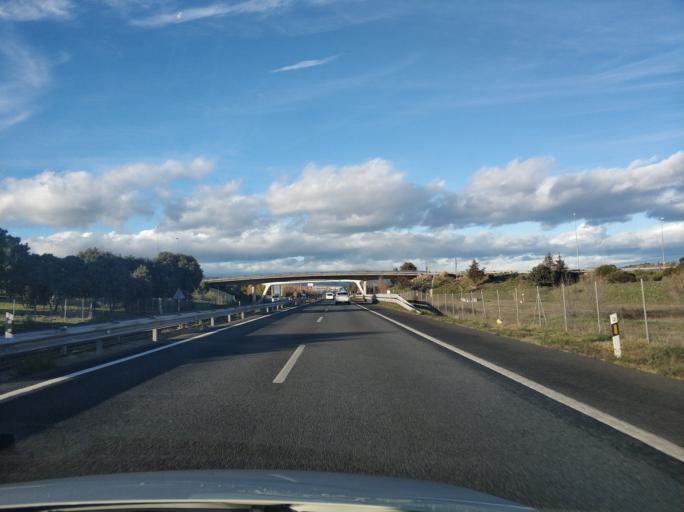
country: ES
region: Madrid
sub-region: Provincia de Madrid
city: San Agustin de Guadalix
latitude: 40.6261
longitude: -3.5869
